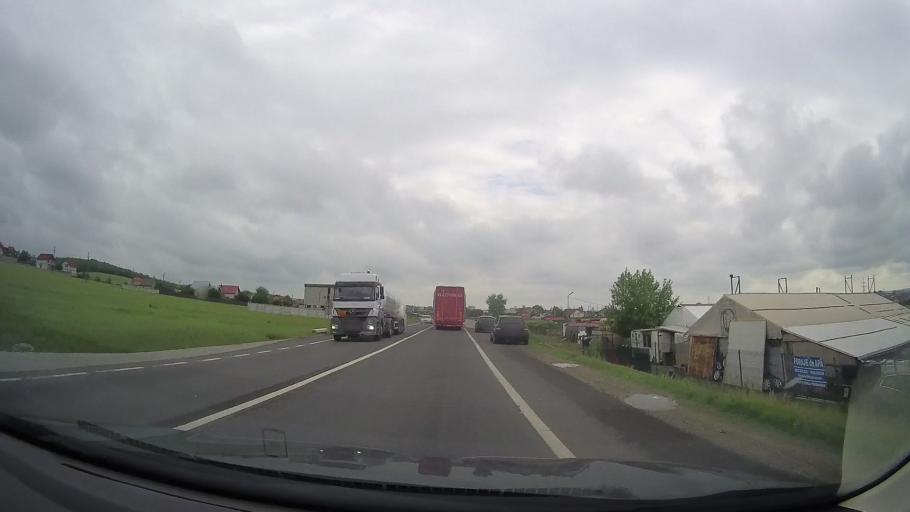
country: RO
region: Dolj
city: Craiova
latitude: 44.3276
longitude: 23.8440
